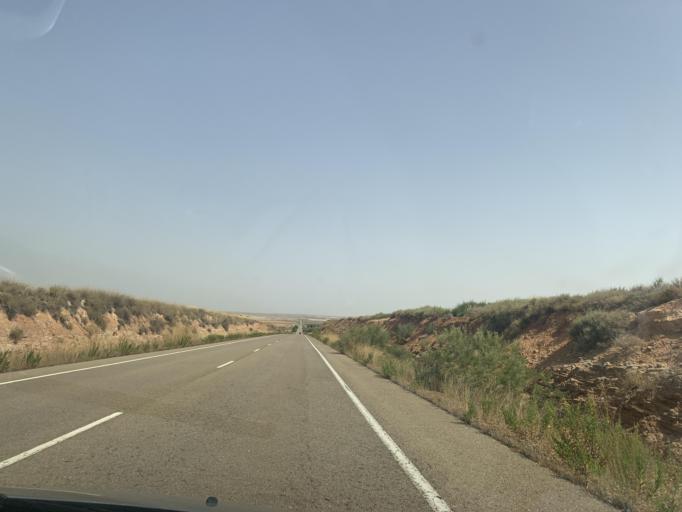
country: ES
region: Aragon
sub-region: Provincia de Zaragoza
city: Belchite
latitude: 41.3399
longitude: -0.7384
